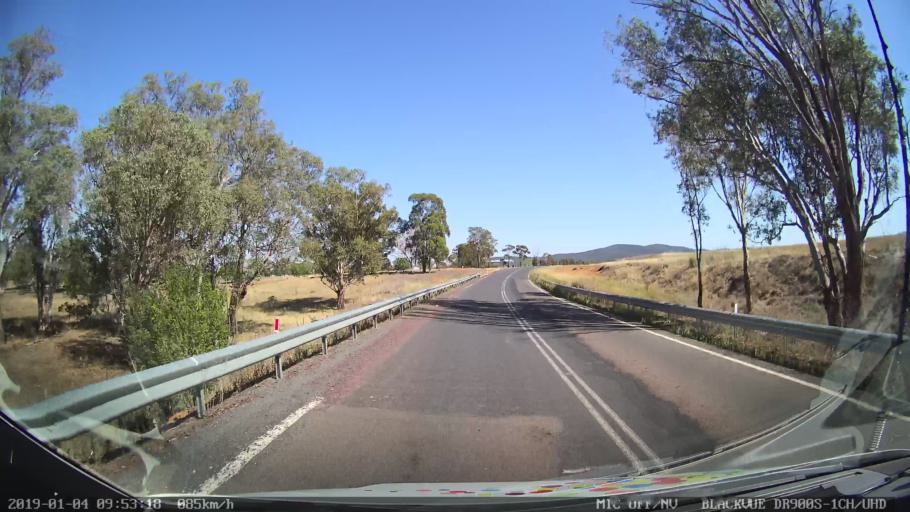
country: AU
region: New South Wales
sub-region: Cabonne
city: Canowindra
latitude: -33.5542
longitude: 148.4207
